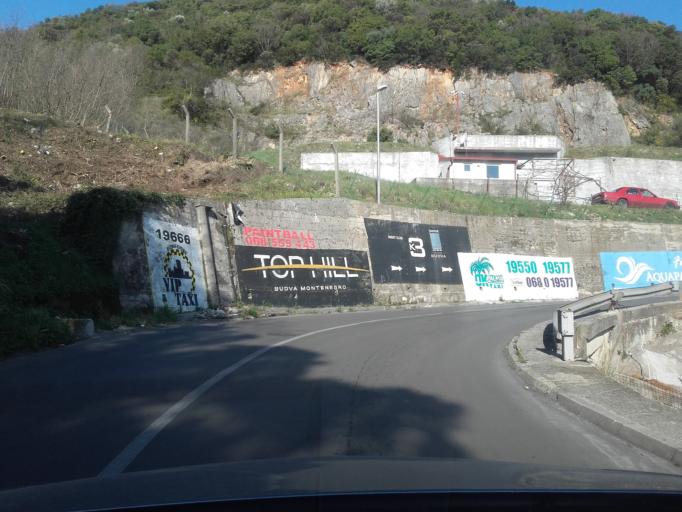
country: ME
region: Budva
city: Budva
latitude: 42.2888
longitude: 18.8287
